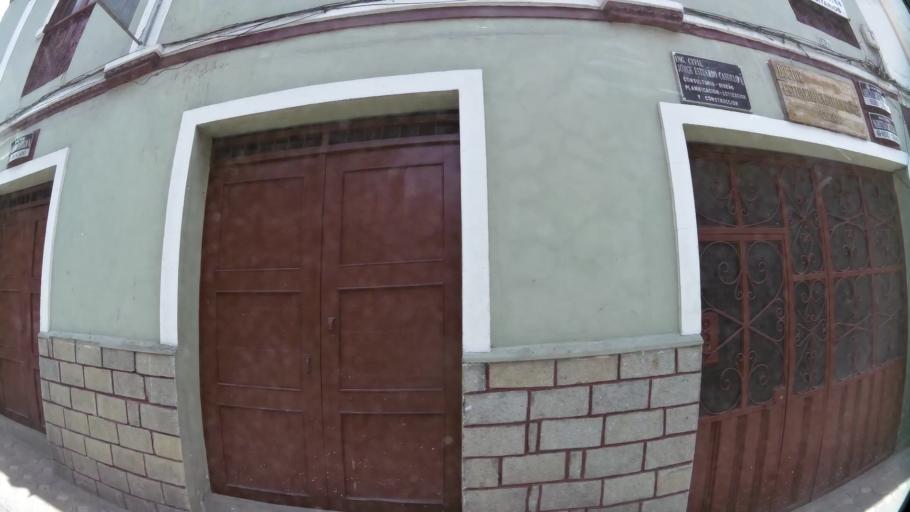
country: EC
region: Azuay
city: Cuenca
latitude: -2.8920
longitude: -79.0019
